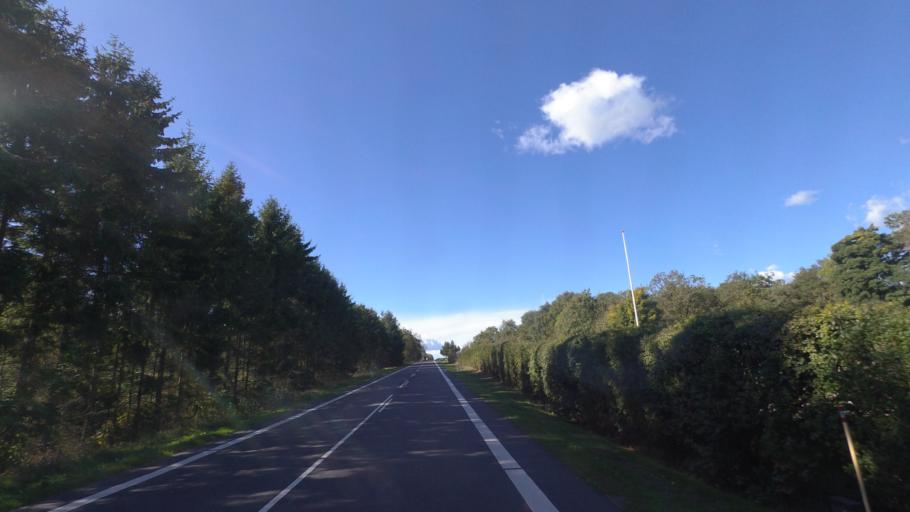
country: DK
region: Capital Region
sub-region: Bornholm Kommune
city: Akirkeby
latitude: 55.0652
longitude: 15.0125
